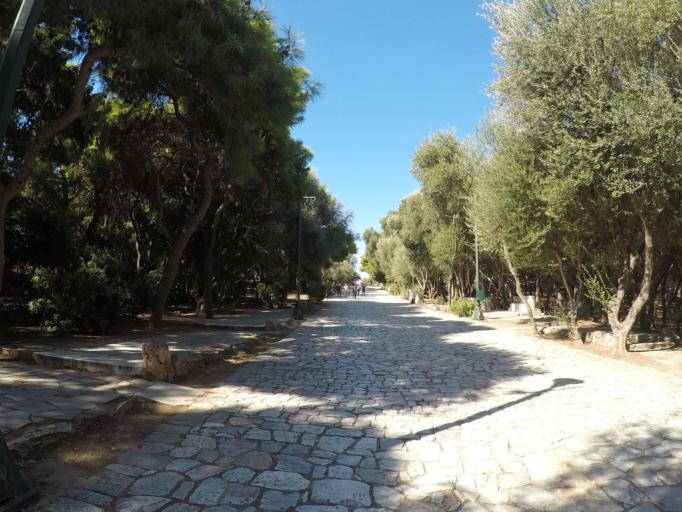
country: GR
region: Attica
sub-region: Nomarchia Athinas
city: Athens
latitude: 37.9701
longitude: 23.7215
